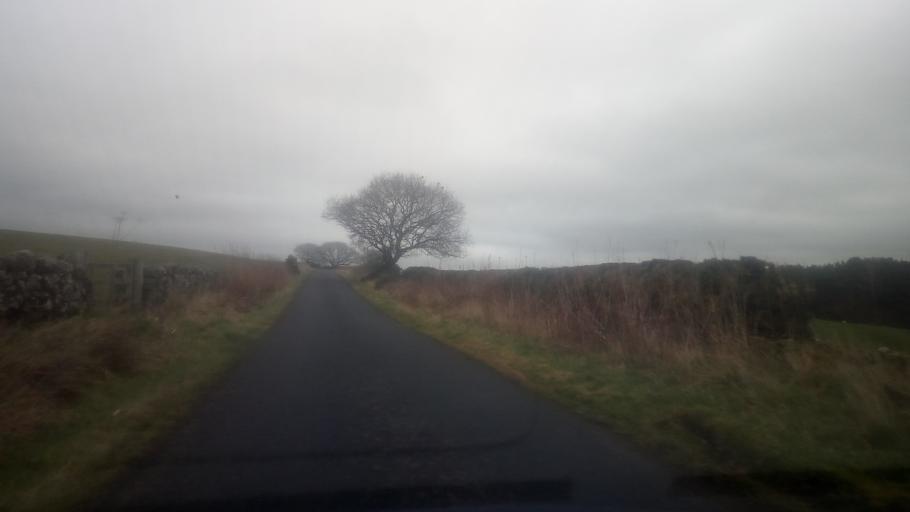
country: GB
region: Scotland
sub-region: The Scottish Borders
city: Kelso
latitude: 55.5492
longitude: -2.4887
